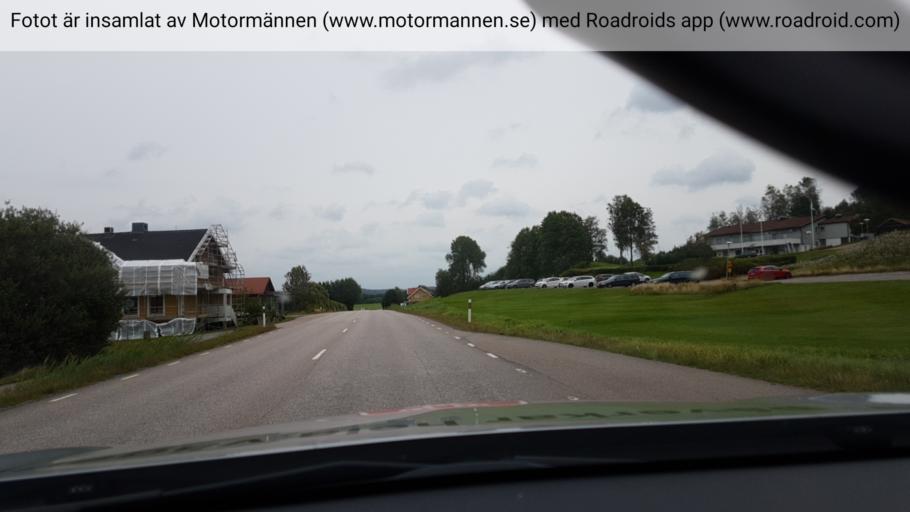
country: SE
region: Vaestra Goetaland
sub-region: Molndal
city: Lindome
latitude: 57.5846
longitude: 12.1144
